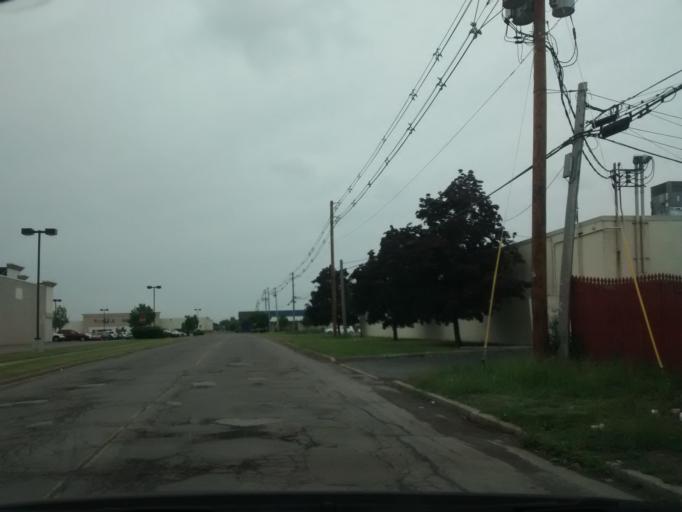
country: US
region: New York
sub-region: Erie County
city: Amherst
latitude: 42.9841
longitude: -78.8218
